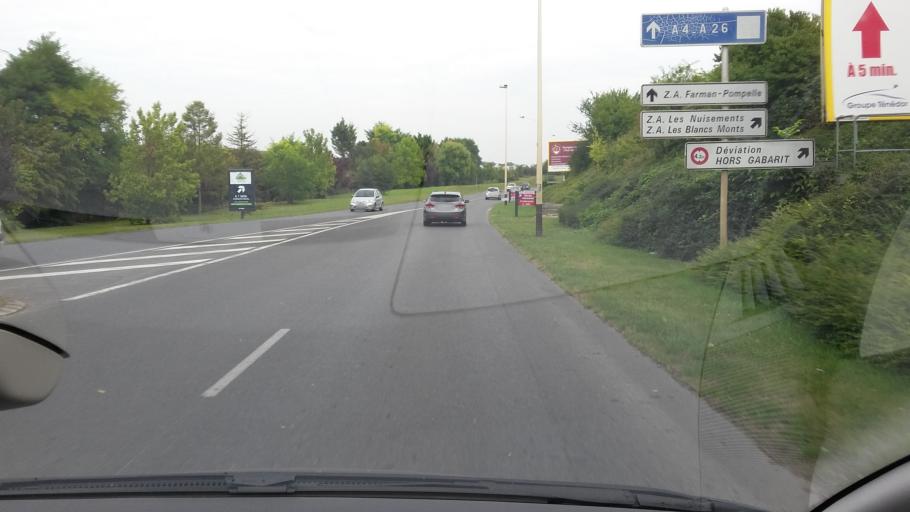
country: FR
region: Champagne-Ardenne
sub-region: Departement de la Marne
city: Cormontreuil
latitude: 49.2169
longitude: 4.0531
